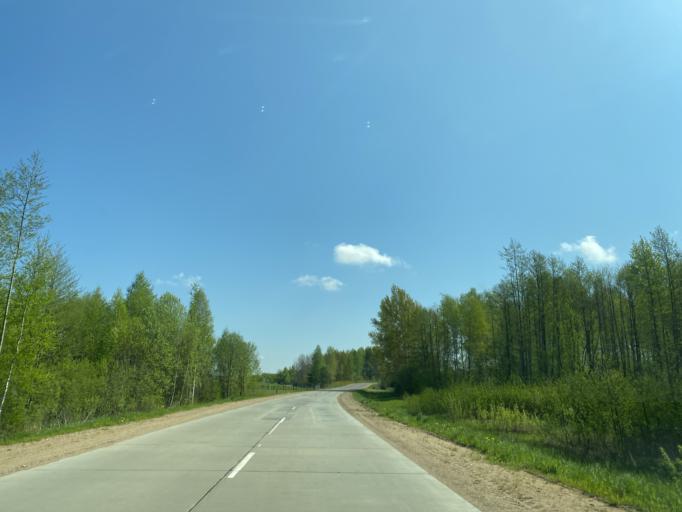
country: BY
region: Minsk
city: Horad Barysaw
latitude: 54.1769
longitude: 28.5363
